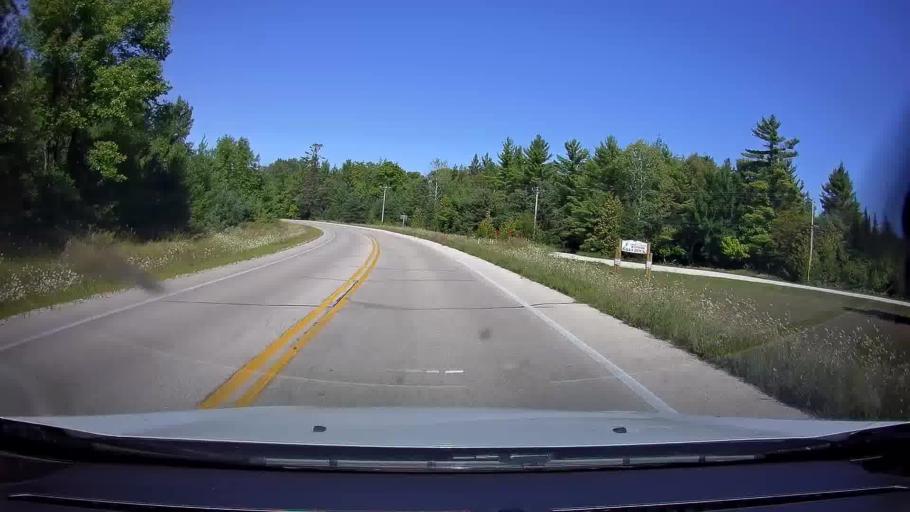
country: US
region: Michigan
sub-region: Delta County
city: Escanaba
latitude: 45.2610
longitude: -87.0204
